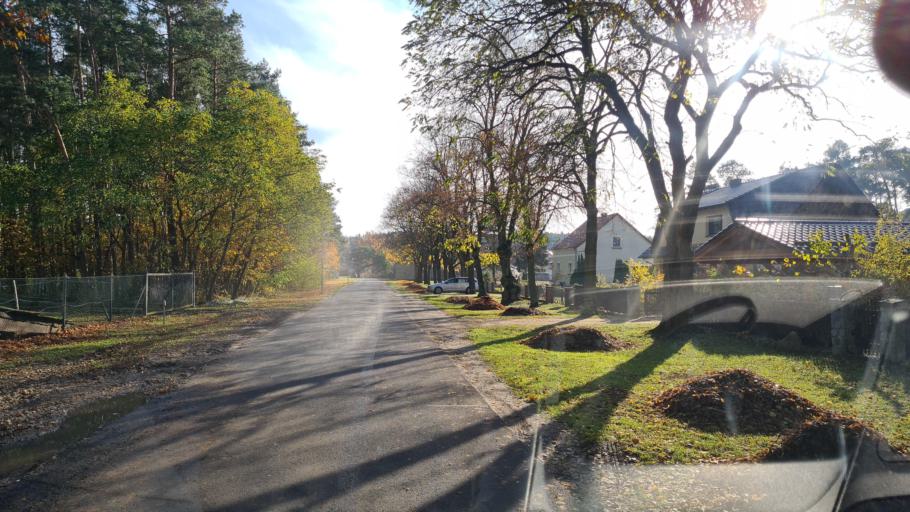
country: DE
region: Brandenburg
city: Golzow
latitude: 52.2821
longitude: 12.6385
